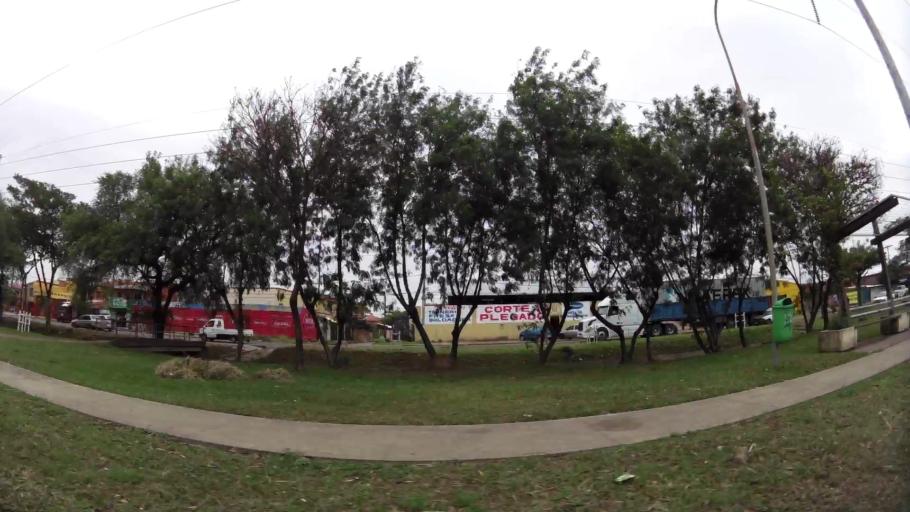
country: BO
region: Santa Cruz
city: Santa Cruz de la Sierra
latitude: -17.7711
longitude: -63.1470
